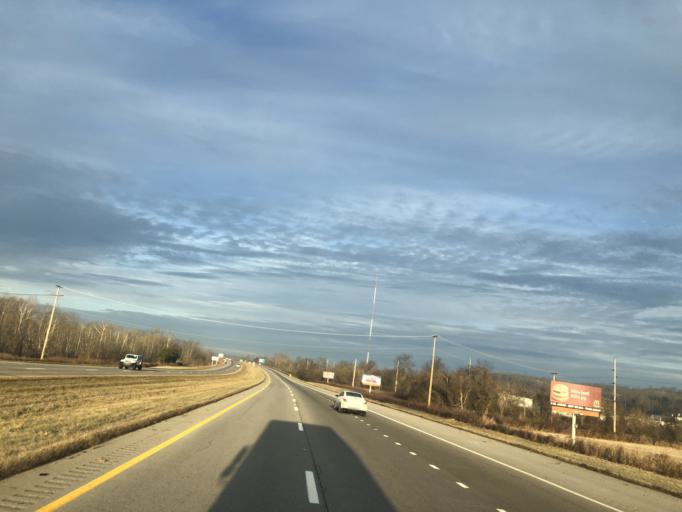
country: US
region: Ohio
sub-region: Hocking County
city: Logan
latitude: 39.5244
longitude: -82.3800
